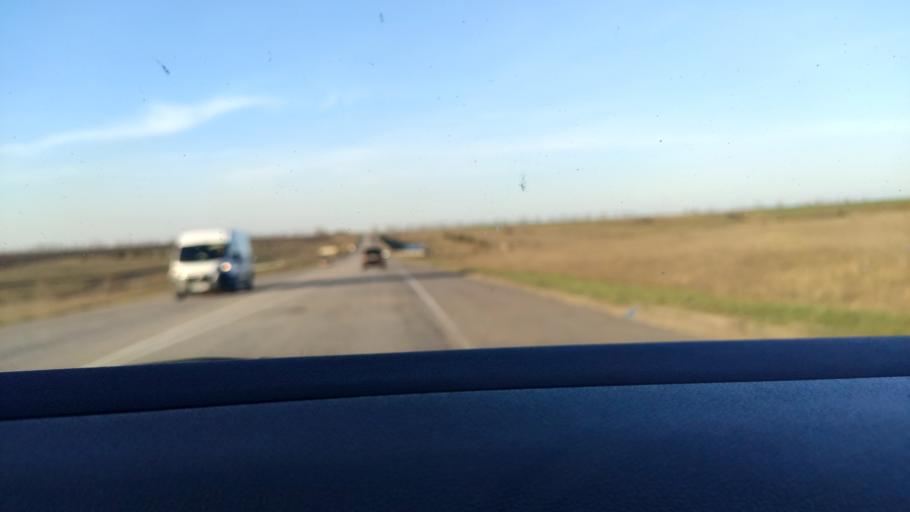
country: RU
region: Voronezj
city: Kolodeznyy
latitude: 51.3849
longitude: 39.2221
